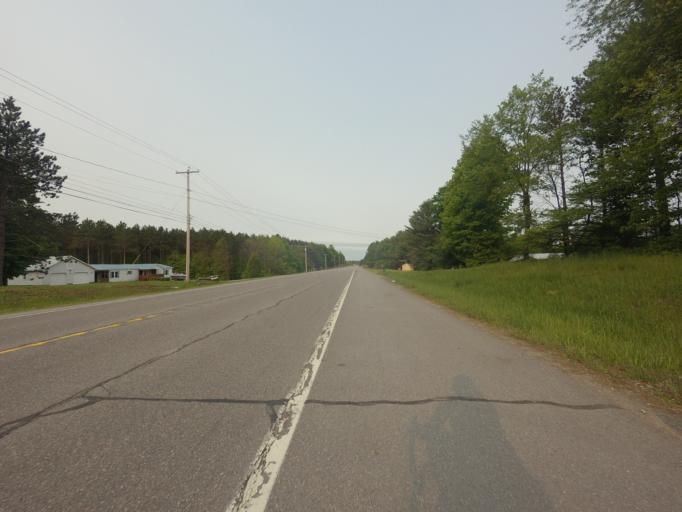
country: US
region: New York
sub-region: Jefferson County
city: Carthage
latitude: 44.0738
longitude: -75.4752
